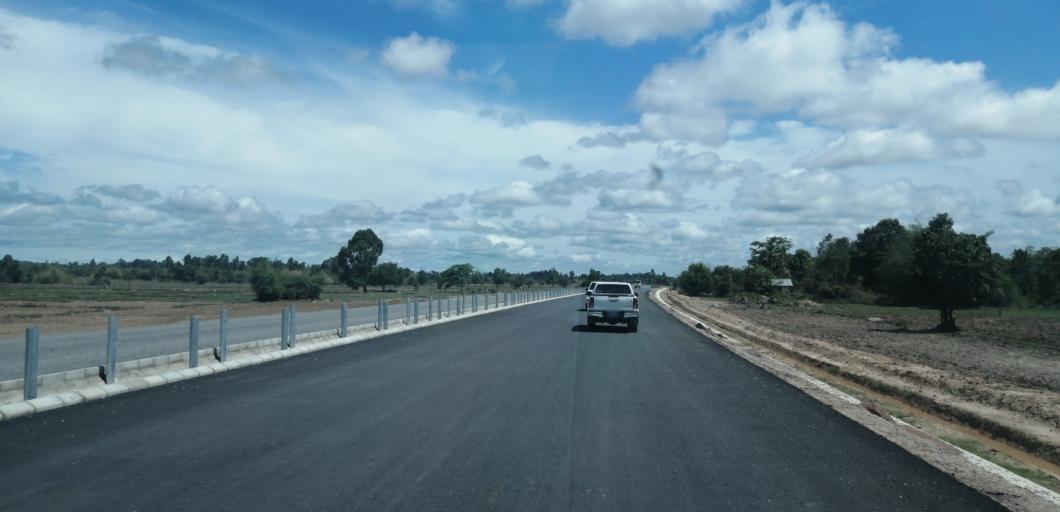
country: LA
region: Vientiane
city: Vientiane
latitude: 18.0683
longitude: 102.5163
